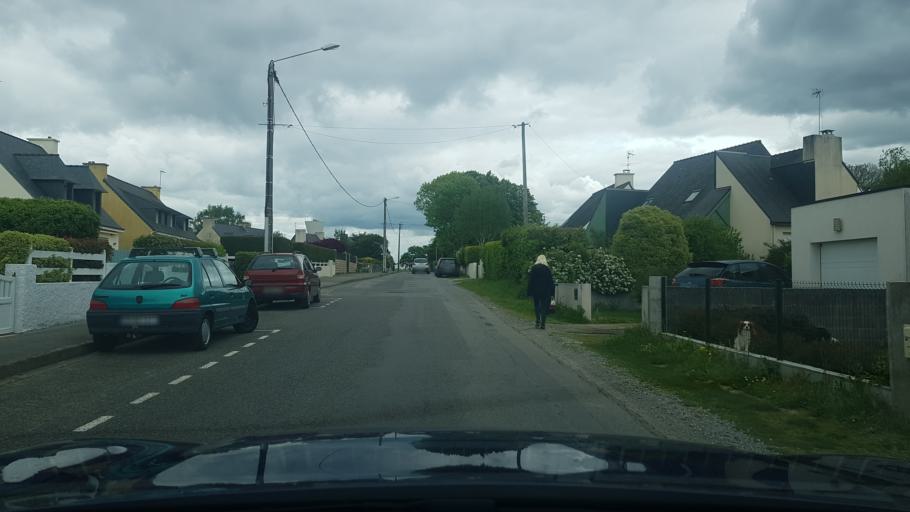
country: FR
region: Brittany
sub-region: Departement du Morbihan
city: Ploemeur
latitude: 47.7467
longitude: -3.4077
